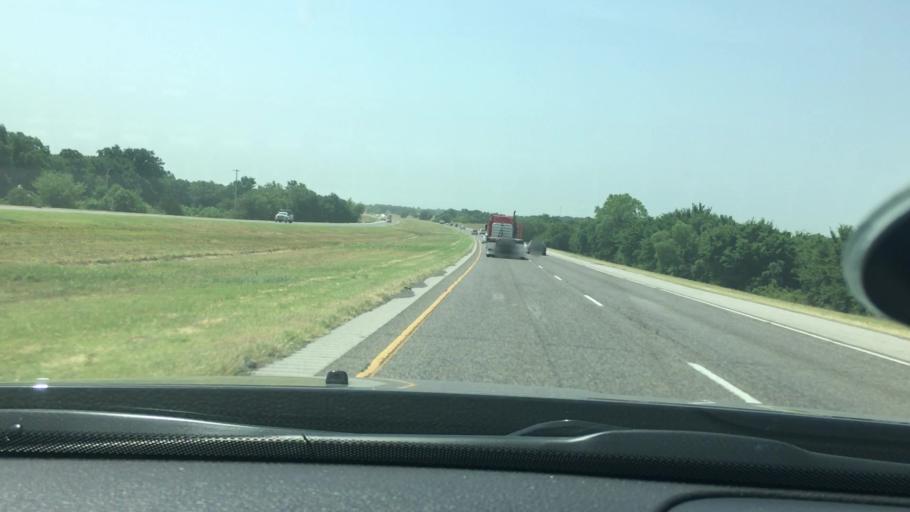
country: US
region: Oklahoma
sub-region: Garvin County
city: Wynnewood
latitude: 34.6051
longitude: -97.2119
